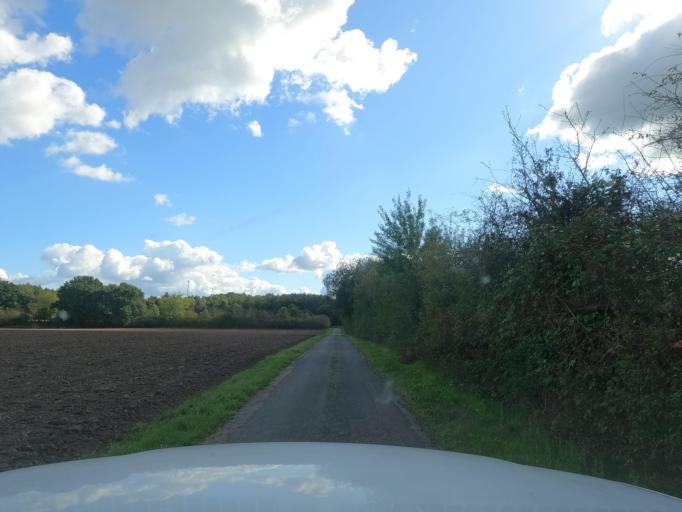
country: DE
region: North Rhine-Westphalia
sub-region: Regierungsbezirk Dusseldorf
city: Hunxe
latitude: 51.6599
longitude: 6.7975
